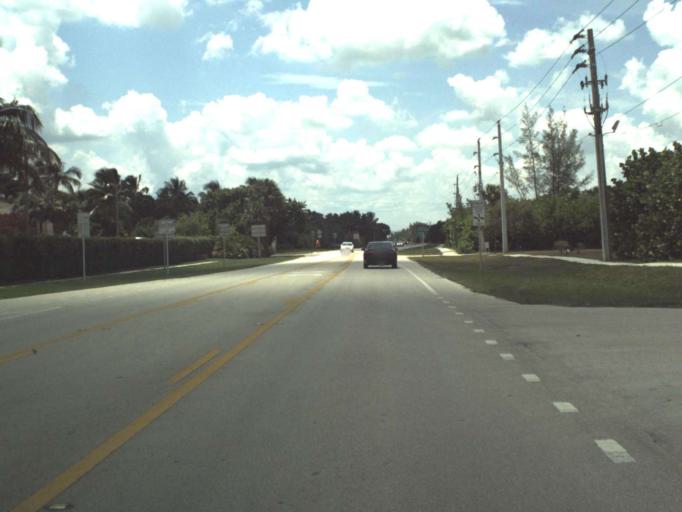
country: US
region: Florida
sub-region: Martin County
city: Jensen Beach
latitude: 27.2639
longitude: -80.2017
